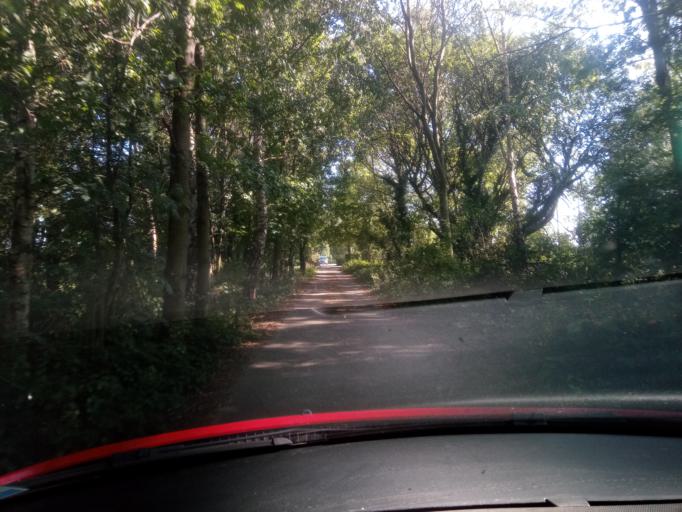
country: GB
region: England
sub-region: North Yorkshire
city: Camblesforth
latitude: 53.7461
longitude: -1.0347
